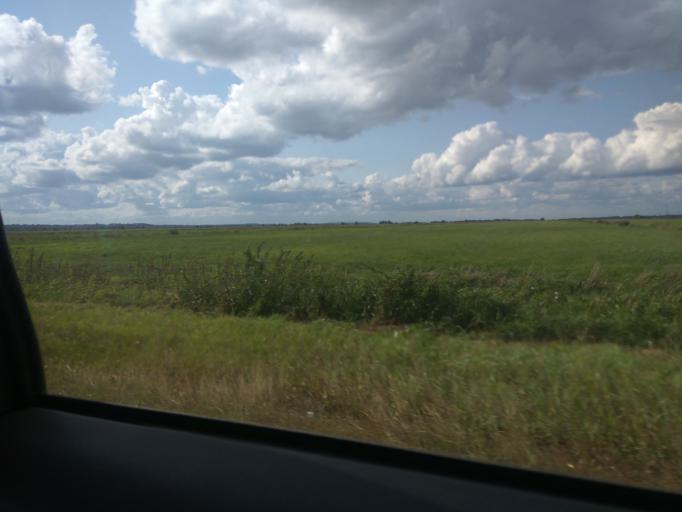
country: RU
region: Moskovskaya
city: Ramenskoye
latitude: 55.5025
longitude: 38.2443
